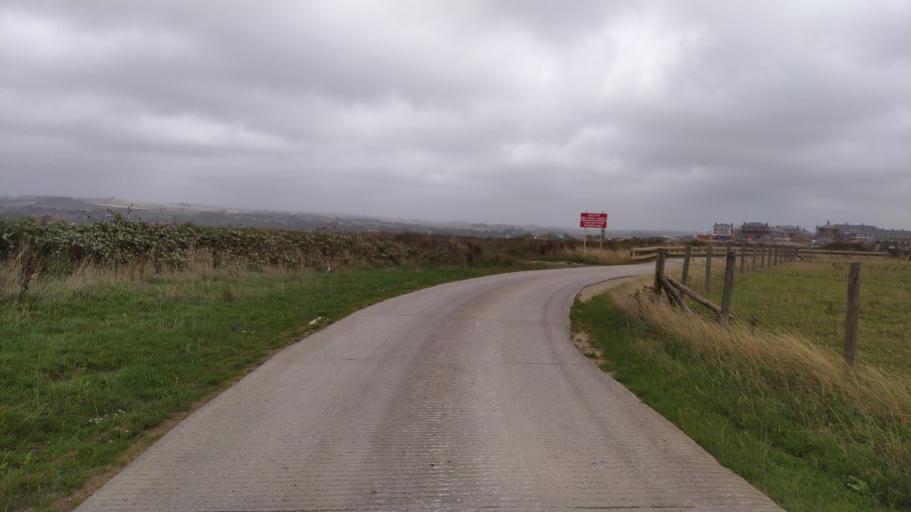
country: GB
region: England
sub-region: Dorset
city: Dorchester
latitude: 50.7168
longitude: -2.4705
